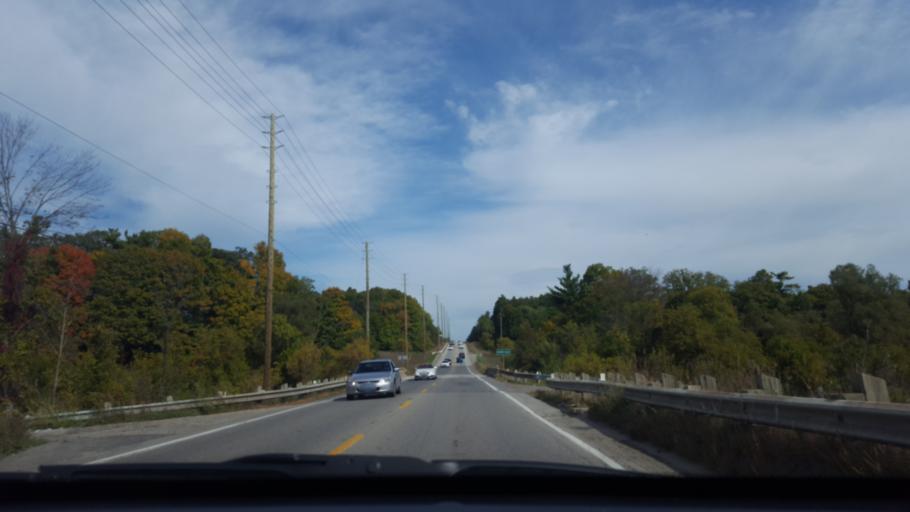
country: CA
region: Ontario
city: Vaughan
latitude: 43.8343
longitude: -79.6095
